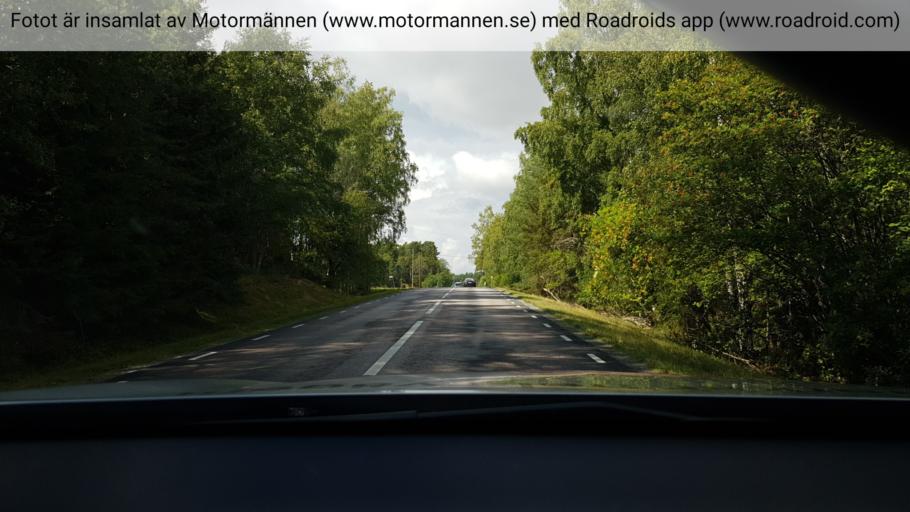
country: SE
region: Stockholm
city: Stenhamra
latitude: 59.3750
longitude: 17.6000
